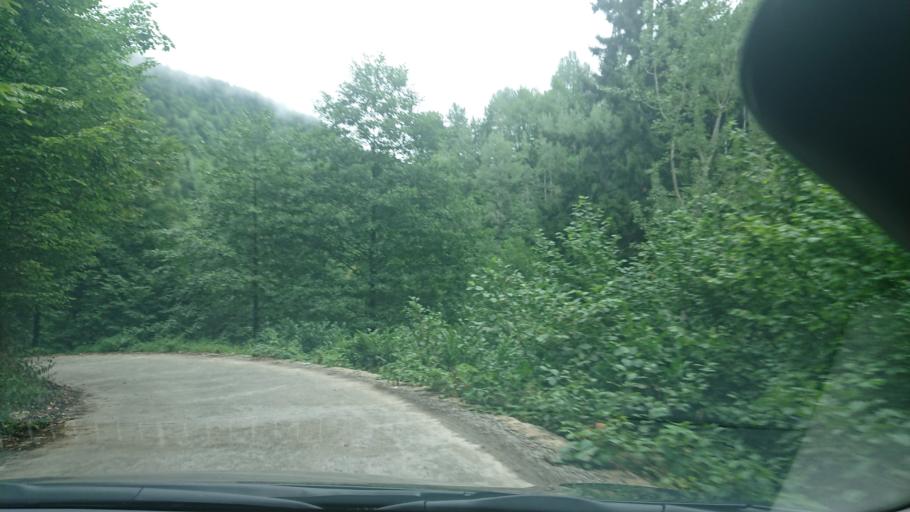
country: TR
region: Gumushane
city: Kurtun
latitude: 40.6741
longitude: 39.0436
